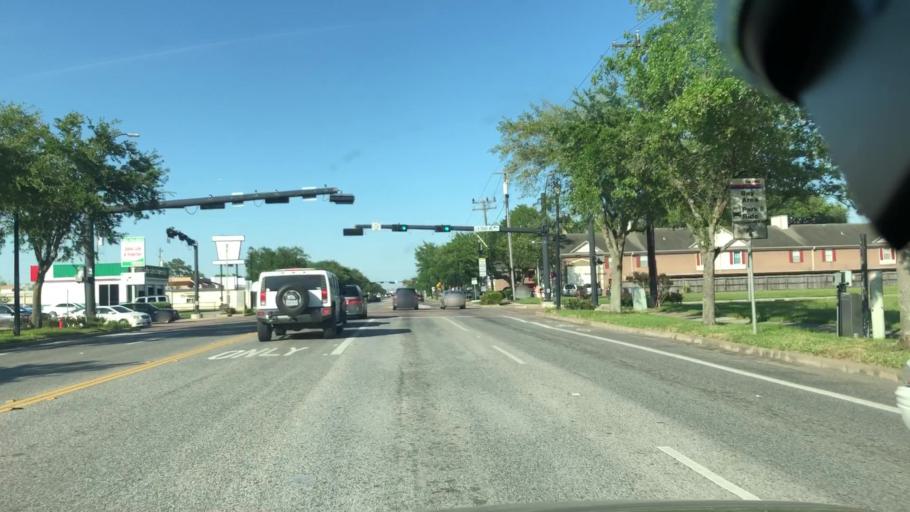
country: US
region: Texas
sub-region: Harris County
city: Webster
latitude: 29.5329
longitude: -95.1246
